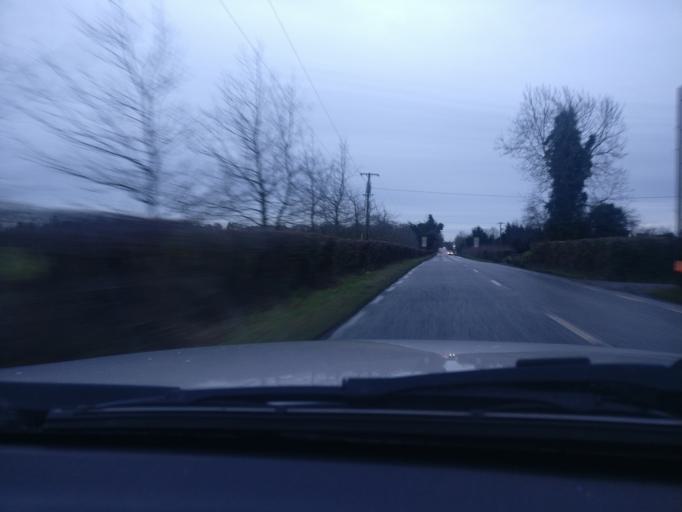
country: IE
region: Leinster
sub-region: An Mhi
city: Navan
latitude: 53.6745
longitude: -6.7437
